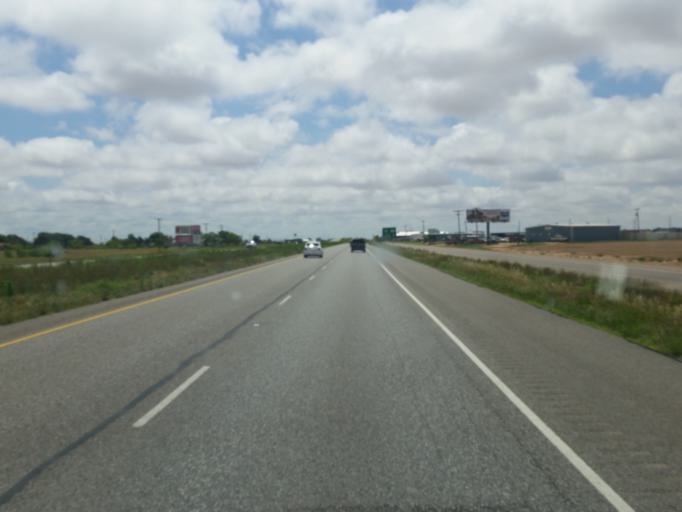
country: US
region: Texas
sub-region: Lubbock County
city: Slaton
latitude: 33.4255
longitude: -101.6526
